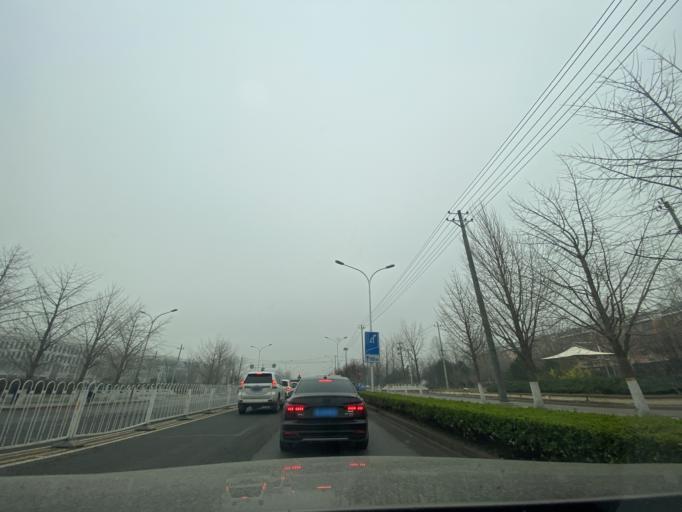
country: CN
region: Beijing
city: Sijiqing
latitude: 39.9719
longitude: 116.2474
